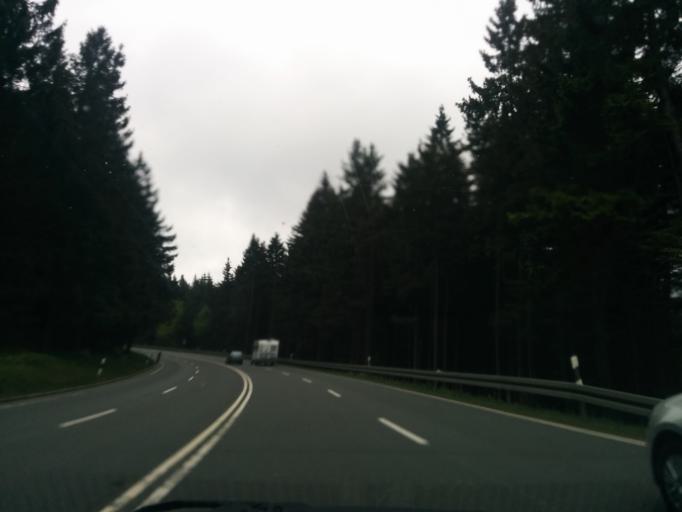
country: DE
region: Lower Saxony
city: Bad Harzburg
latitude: 51.8413
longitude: 10.5277
